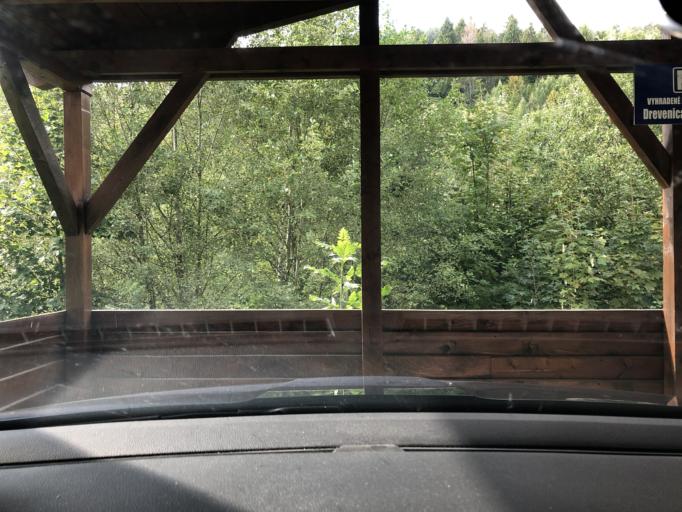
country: SK
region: Zilinsky
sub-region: Okres Zilina
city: Terchova
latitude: 49.2824
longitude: 19.0535
